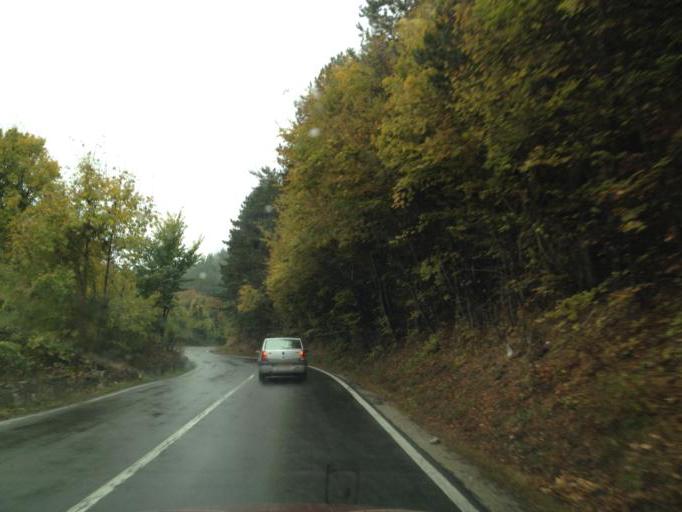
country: RO
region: Arges
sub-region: Comuna Dragoslavele
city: Dragoslavele
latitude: 45.3036
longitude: 25.1546
